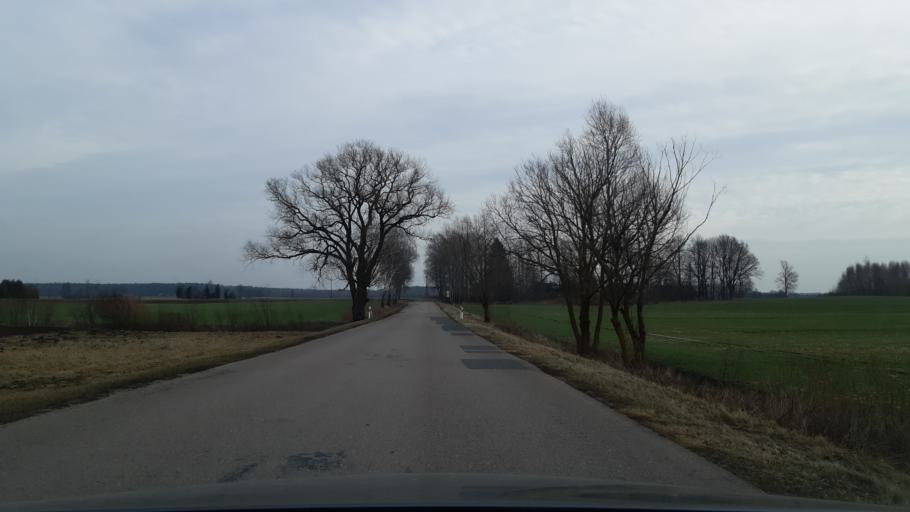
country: LT
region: Marijampoles apskritis
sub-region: Marijampole Municipality
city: Marijampole
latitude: 54.7176
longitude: 23.3274
